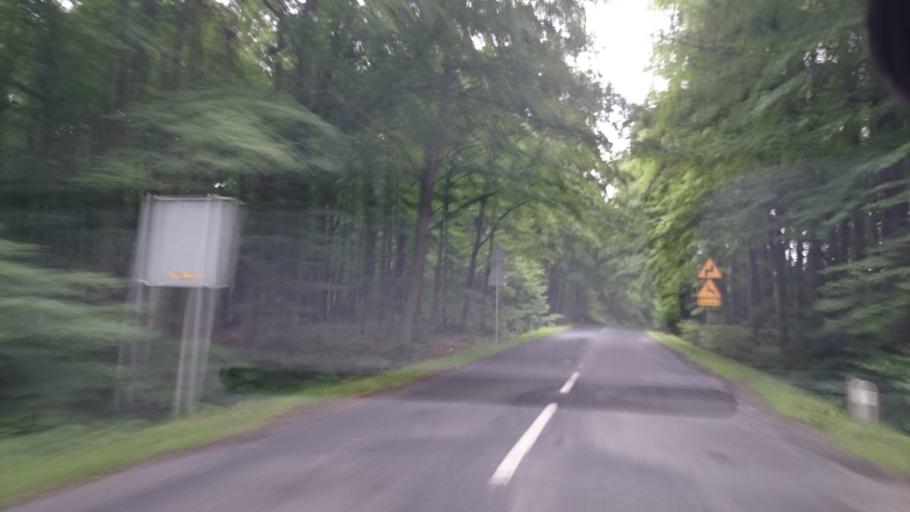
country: PL
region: Lower Silesian Voivodeship
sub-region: Powiat strzelinski
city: Przeworno
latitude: 50.6537
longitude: 17.2339
